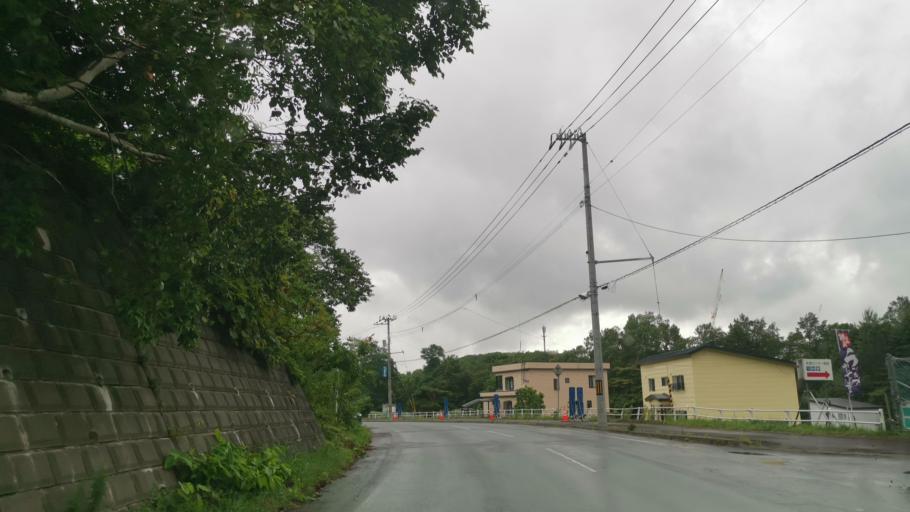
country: JP
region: Hokkaido
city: Sapporo
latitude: 42.9647
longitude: 141.3598
